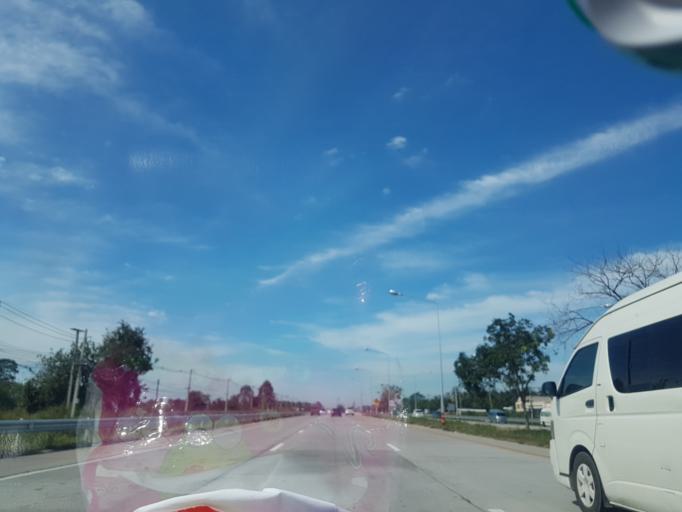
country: TH
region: Chon Buri
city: Phatthaya
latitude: 12.9393
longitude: 100.9960
